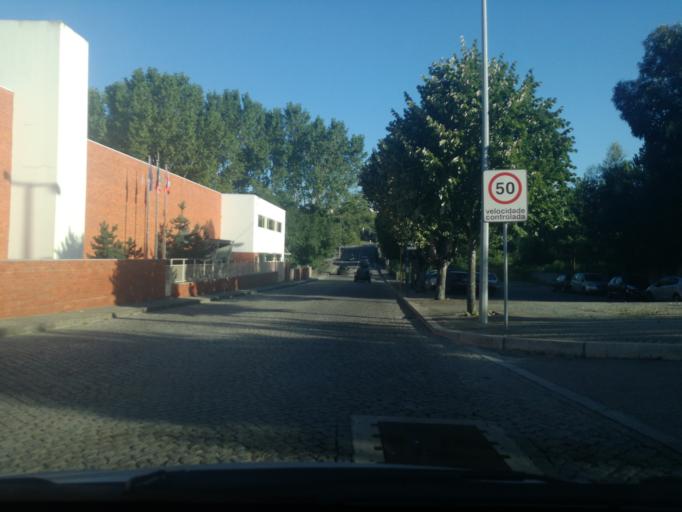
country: PT
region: Porto
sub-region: Maia
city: Milheiros
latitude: 41.2159
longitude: -8.5969
